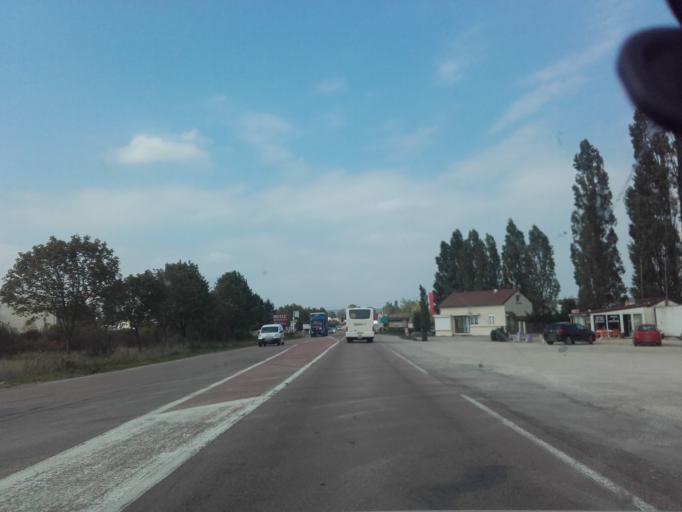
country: FR
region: Bourgogne
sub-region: Departement de Saone-et-Loire
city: Chagny
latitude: 46.8960
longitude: 4.7631
